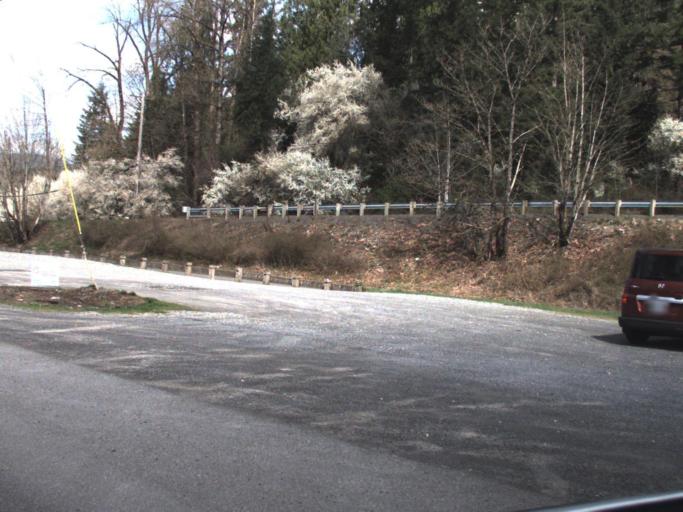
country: US
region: Washington
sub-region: King County
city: Maple Valley
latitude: 47.4093
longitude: -122.0386
